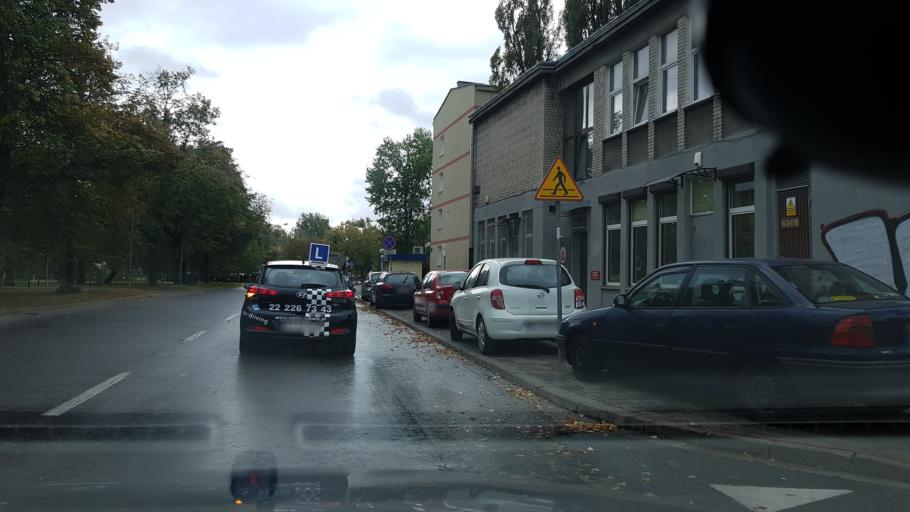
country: PL
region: Masovian Voivodeship
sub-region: Warszawa
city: Bielany
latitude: 52.2755
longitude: 20.9534
